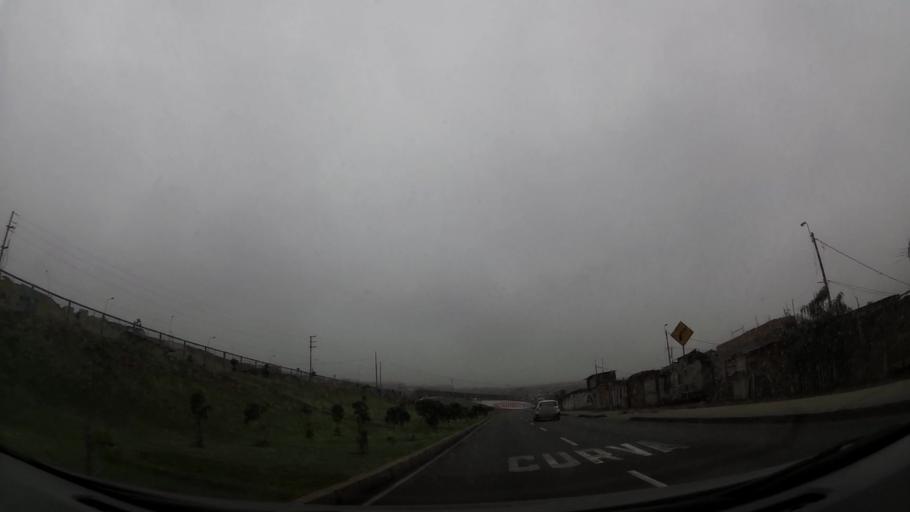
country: PE
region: Lima
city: Ventanilla
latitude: -11.8550
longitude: -77.1298
